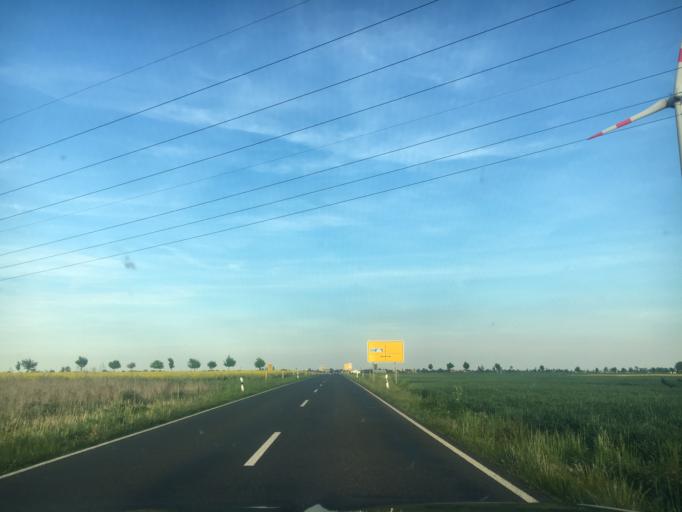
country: DE
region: Saxony-Anhalt
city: Raguhn
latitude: 51.7121
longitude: 12.2443
